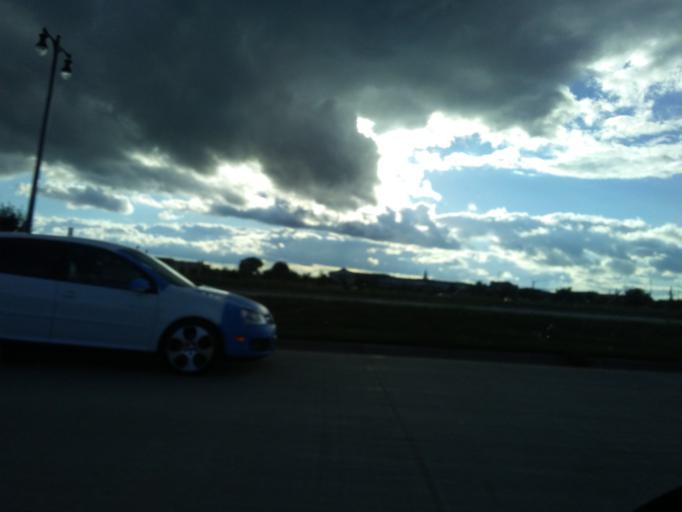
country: US
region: Wisconsin
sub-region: Dane County
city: Sun Prairie
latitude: 43.1653
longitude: -89.2689
